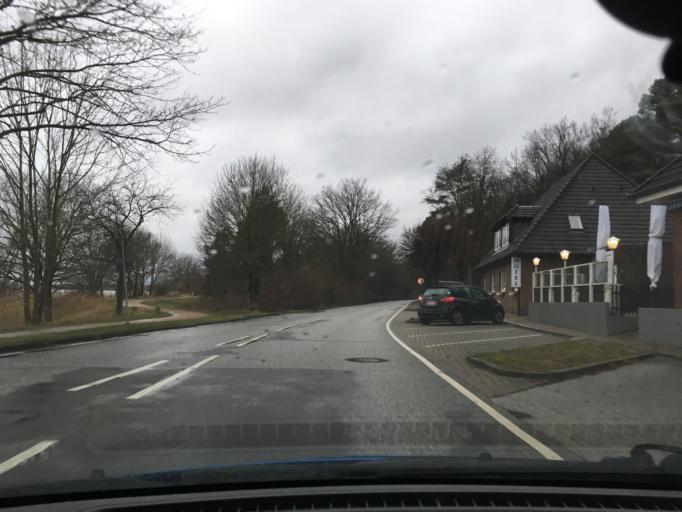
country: DE
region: Lower Saxony
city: Tespe
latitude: 53.4120
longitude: 10.4033
